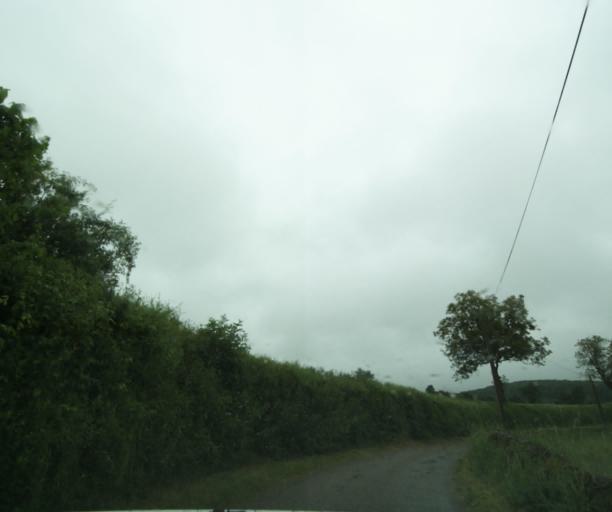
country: FR
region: Bourgogne
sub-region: Departement de Saone-et-Loire
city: Charolles
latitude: 46.3982
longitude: 4.2708
